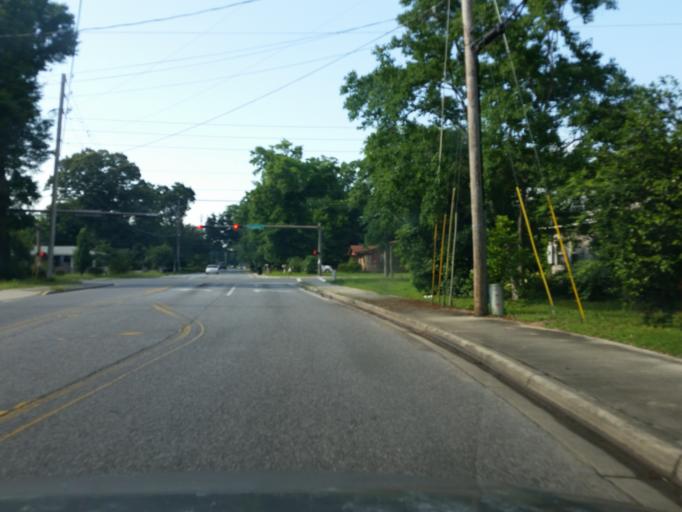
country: US
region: Florida
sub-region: Escambia County
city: Ferry Pass
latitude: 30.4947
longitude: -87.1965
